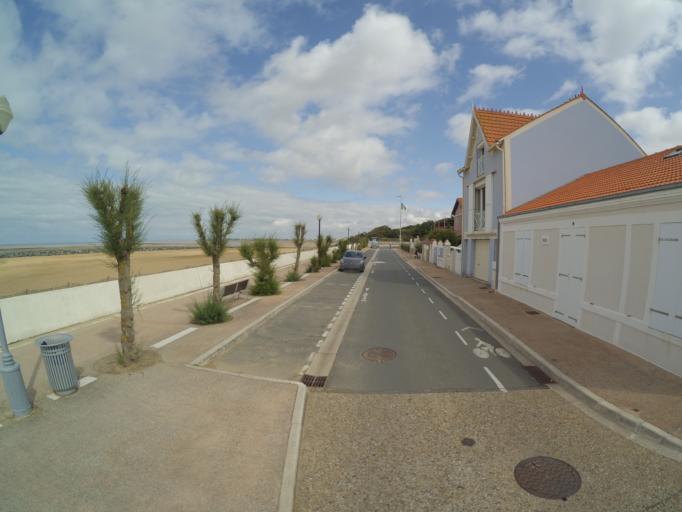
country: FR
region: Poitou-Charentes
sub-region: Departement de la Charente-Maritime
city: Chatelaillon-Plage
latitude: 46.0820
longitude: -1.0962
